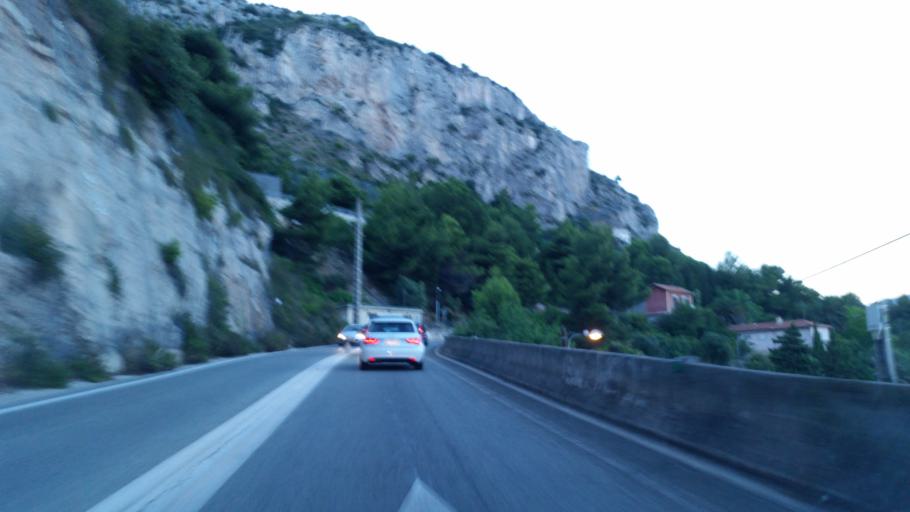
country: MC
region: Commune de Monaco
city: Saint-Roman
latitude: 43.7581
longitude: 7.4439
